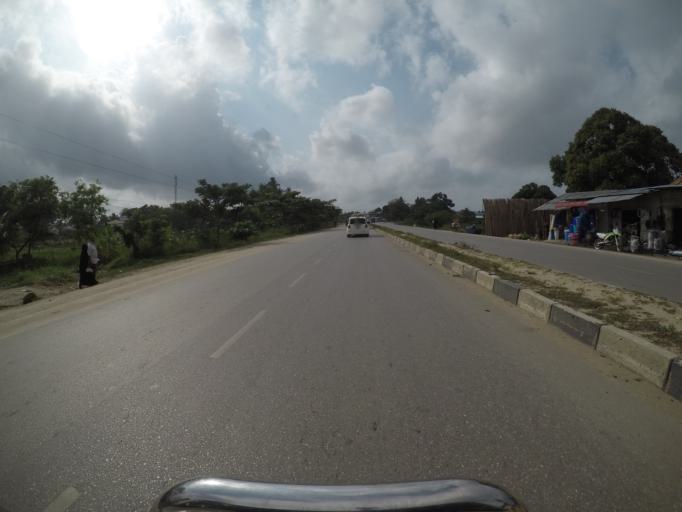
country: TZ
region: Zanzibar Urban/West
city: Zanzibar
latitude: -6.1861
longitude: 39.2380
